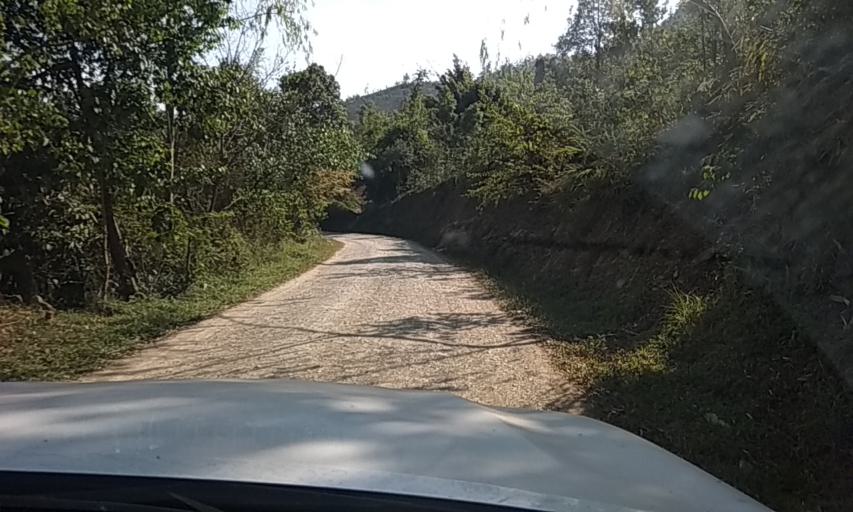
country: LA
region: Phongsali
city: Phongsali
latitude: 21.6554
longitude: 102.0909
